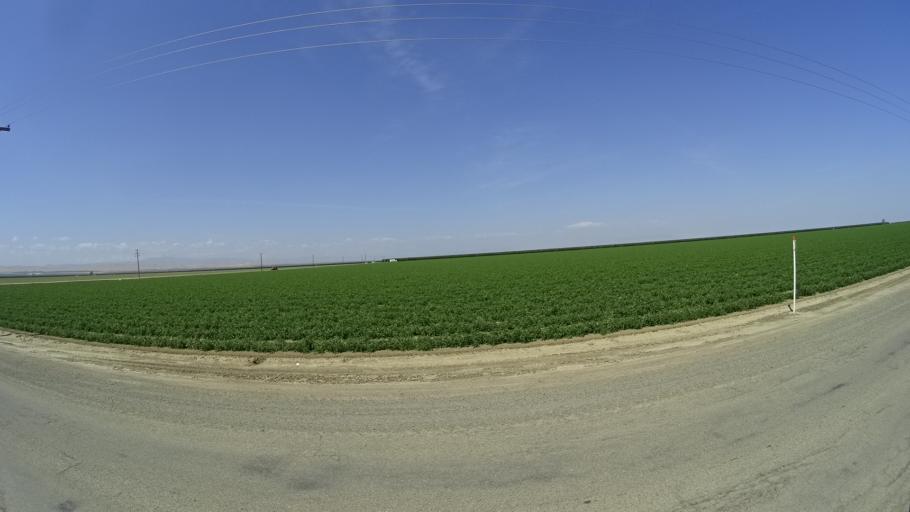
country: US
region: California
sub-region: Kings County
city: Kettleman City
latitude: 36.1243
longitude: -120.0037
